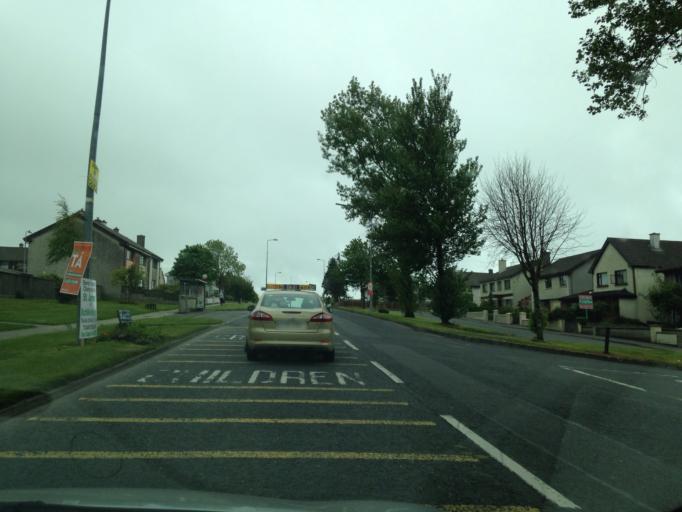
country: IE
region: Connaught
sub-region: County Galway
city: Gaillimh
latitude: 53.2833
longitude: -9.0104
